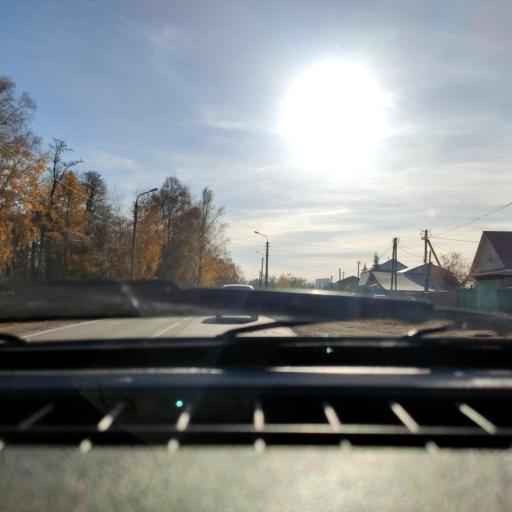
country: RU
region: Bashkortostan
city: Ufa
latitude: 54.8138
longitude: 56.1635
